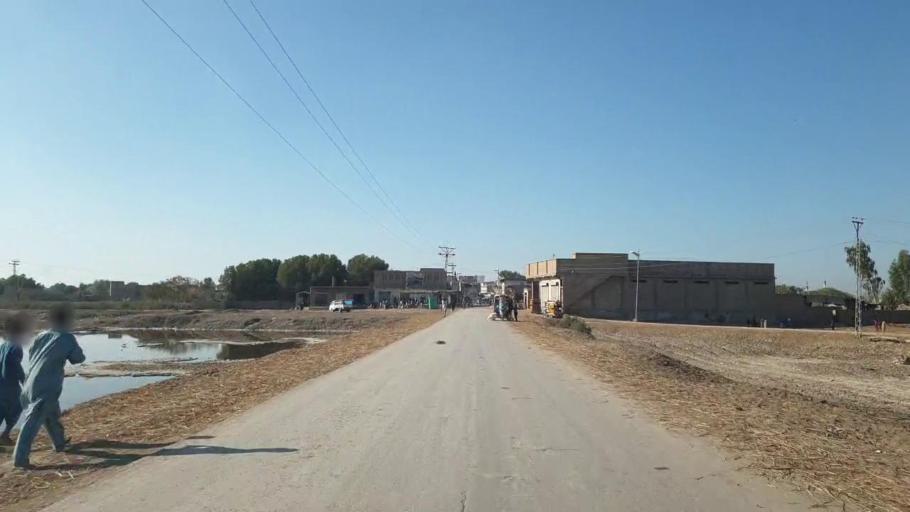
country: PK
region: Sindh
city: New Badah
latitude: 27.3267
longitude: 68.0294
